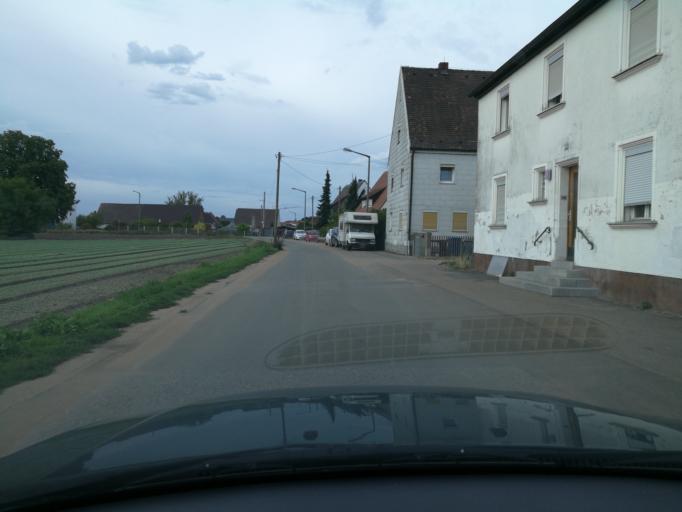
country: DE
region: Bavaria
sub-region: Regierungsbezirk Mittelfranken
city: Wetzendorf
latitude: 49.4944
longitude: 11.0446
